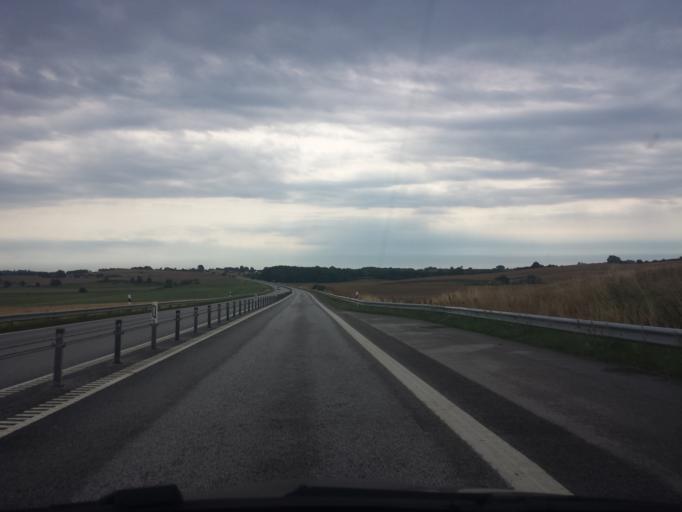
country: SE
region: Skane
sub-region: Ystads Kommun
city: Ystad
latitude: 55.4638
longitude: 13.7190
